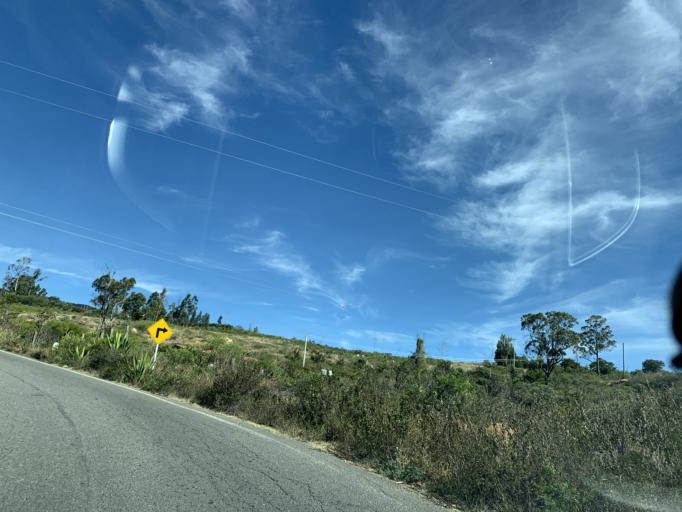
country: CO
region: Boyaca
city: Santa Sofia
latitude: 5.6883
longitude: -73.5882
